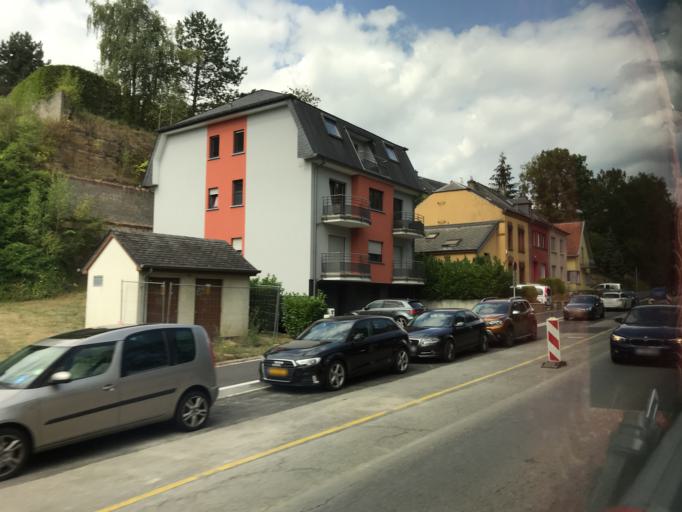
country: LU
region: Luxembourg
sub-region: Canton de Luxembourg
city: Hesperange
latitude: 49.5818
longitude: 6.1485
